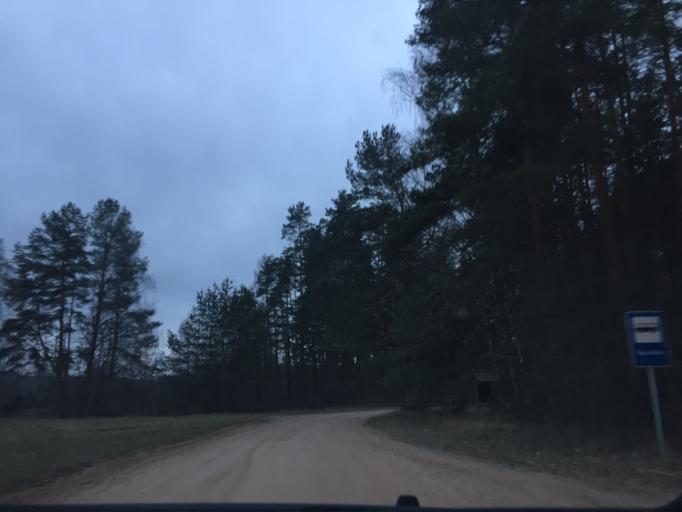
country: LV
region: Cesu Rajons
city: Cesis
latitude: 57.3542
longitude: 25.2605
